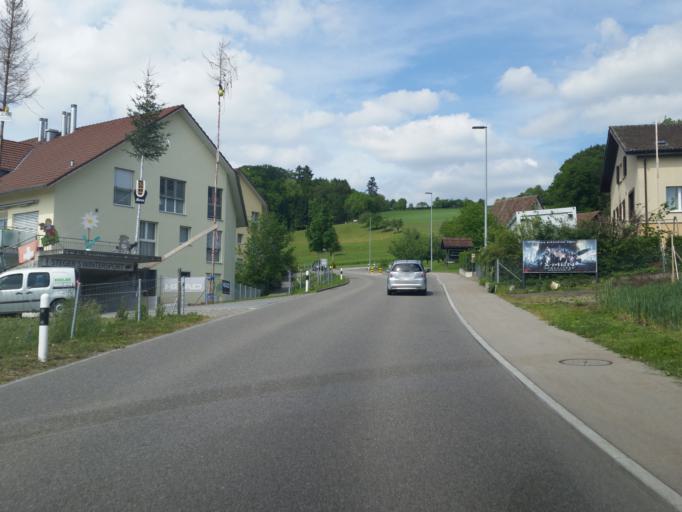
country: CH
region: Aargau
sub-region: Bezirk Bremgarten
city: Unterlunkhofen
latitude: 47.3258
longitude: 8.3793
